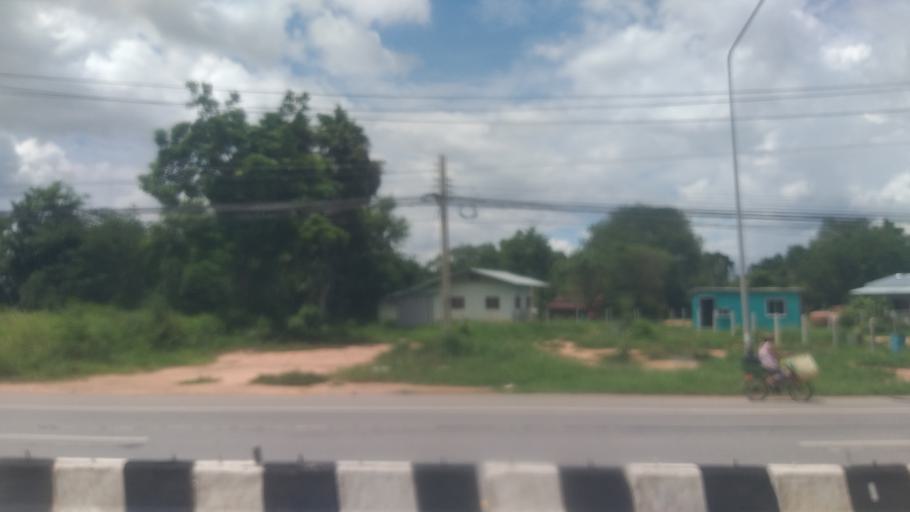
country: TH
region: Nakhon Ratchasima
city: Non Thai
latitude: 15.1428
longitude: 102.1038
